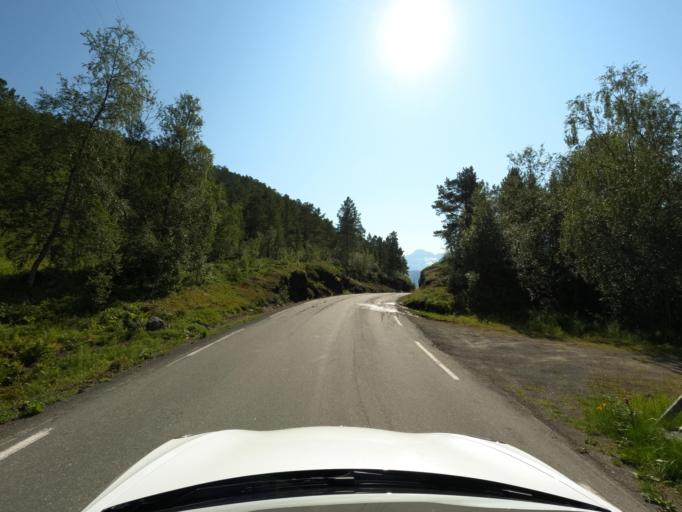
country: NO
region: Nordland
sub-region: Narvik
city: Narvik
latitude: 68.3649
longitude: 17.2620
